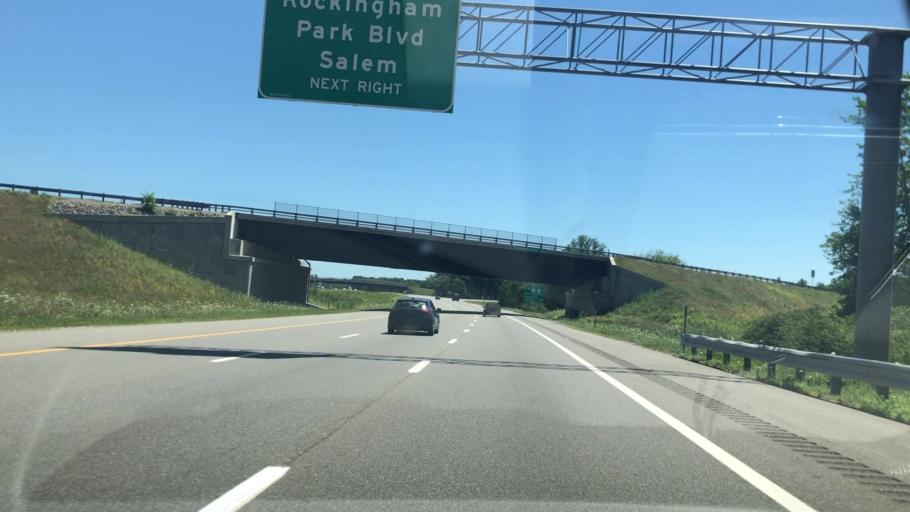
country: US
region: New Hampshire
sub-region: Rockingham County
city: Salem
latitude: 42.7615
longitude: -71.2347
